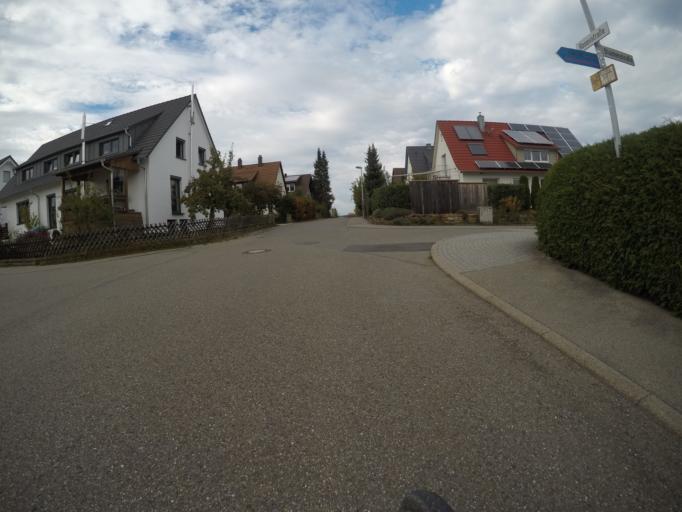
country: DE
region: Baden-Wuerttemberg
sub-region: Regierungsbezirk Stuttgart
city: Nufringen
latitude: 48.6243
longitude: 8.8915
